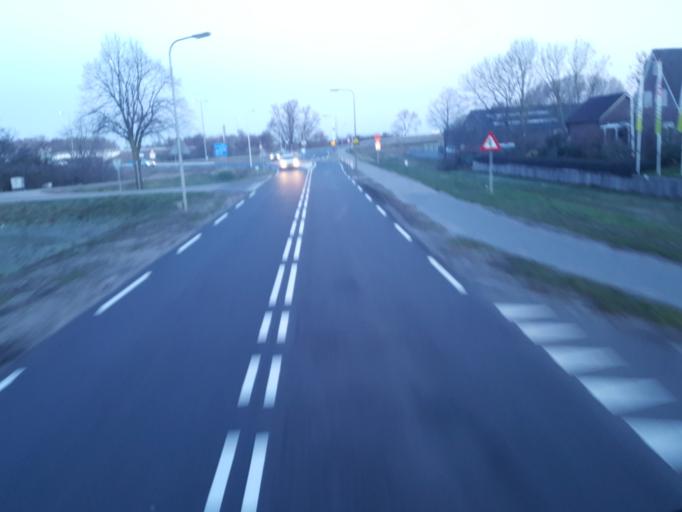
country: NL
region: Overijssel
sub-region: Gemeente Zwartewaterland
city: Hasselt
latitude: 52.5886
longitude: 6.0857
